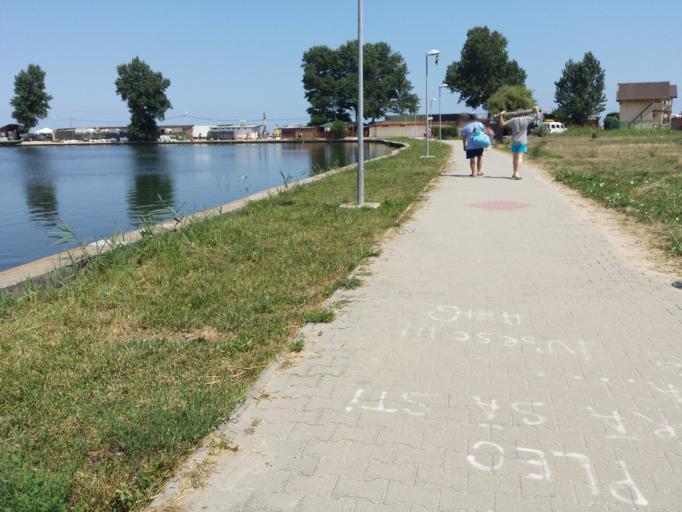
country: RO
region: Constanta
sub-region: Comuna Douazeci si Trei August
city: Douazeci si Trei August
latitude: 43.8600
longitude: 28.6046
